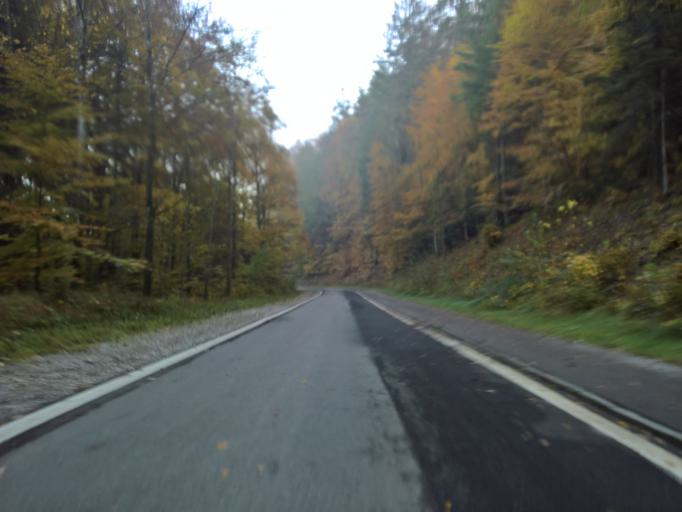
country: CH
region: Bern
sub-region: Bern-Mittelland District
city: Bern
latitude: 46.9657
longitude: 7.4188
